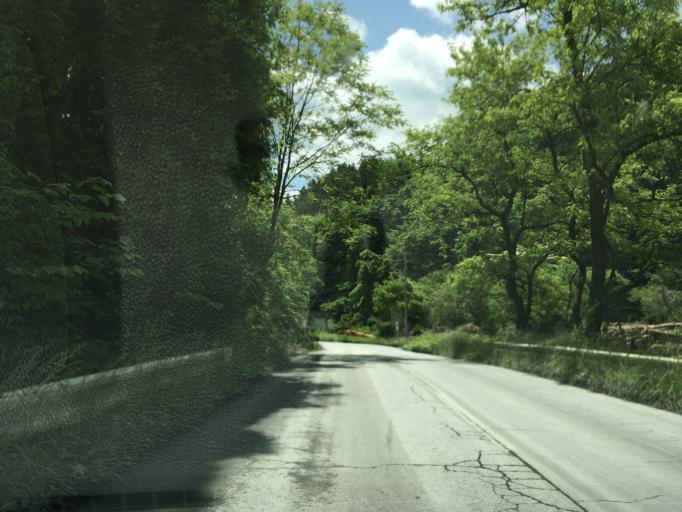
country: JP
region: Miyagi
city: Wakuya
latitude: 38.6601
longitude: 141.3223
